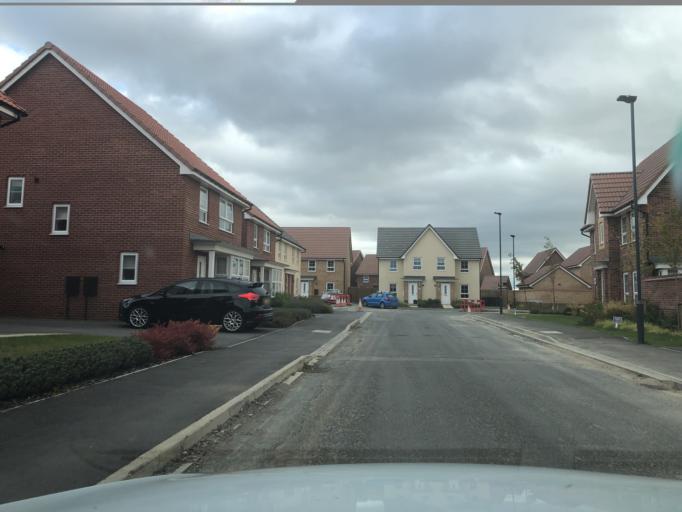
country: GB
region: England
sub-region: North Yorkshire
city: Northallerton
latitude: 54.3441
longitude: -1.4439
